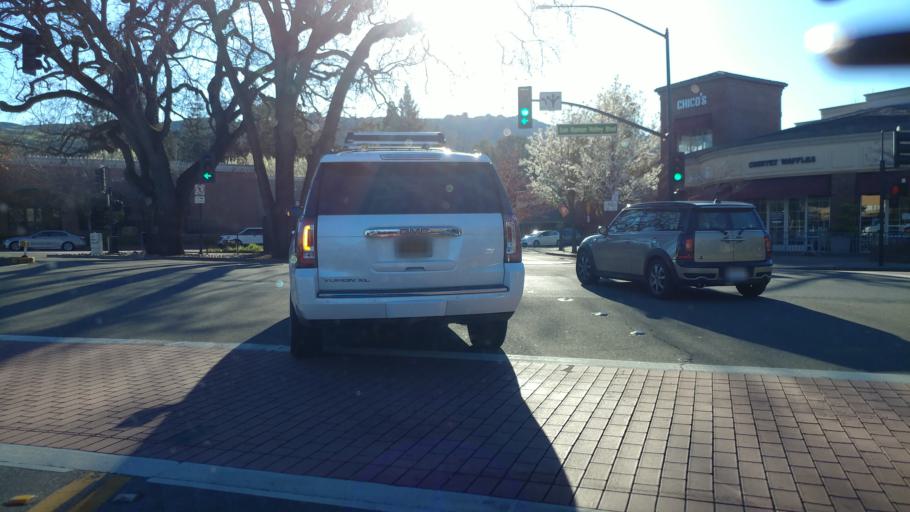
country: US
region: California
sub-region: Contra Costa County
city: Danville
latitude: 37.8192
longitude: -121.9963
